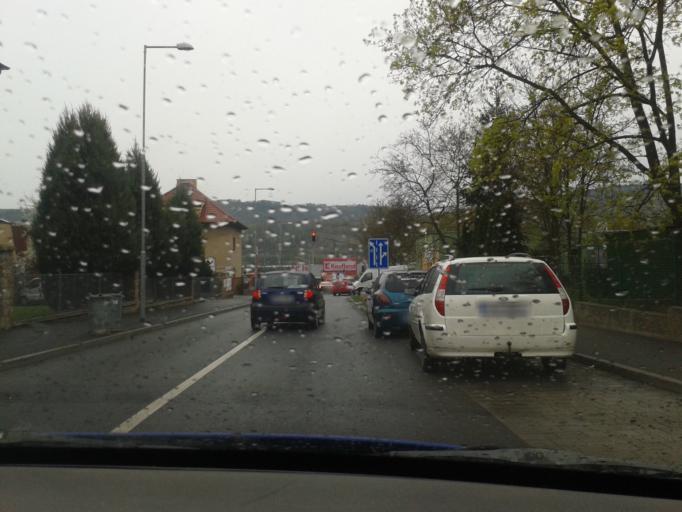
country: CZ
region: Central Bohemia
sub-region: Okres Beroun
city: Beroun
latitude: 49.9591
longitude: 14.0591
